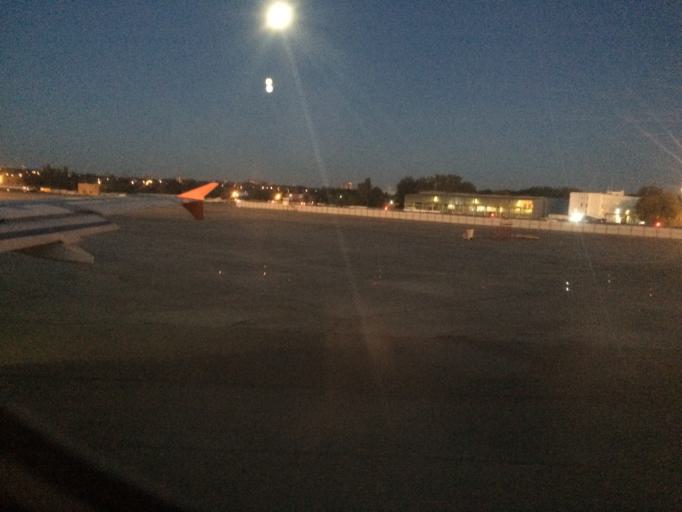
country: RU
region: Rostov
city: Aksay
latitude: 47.2526
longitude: 39.8046
